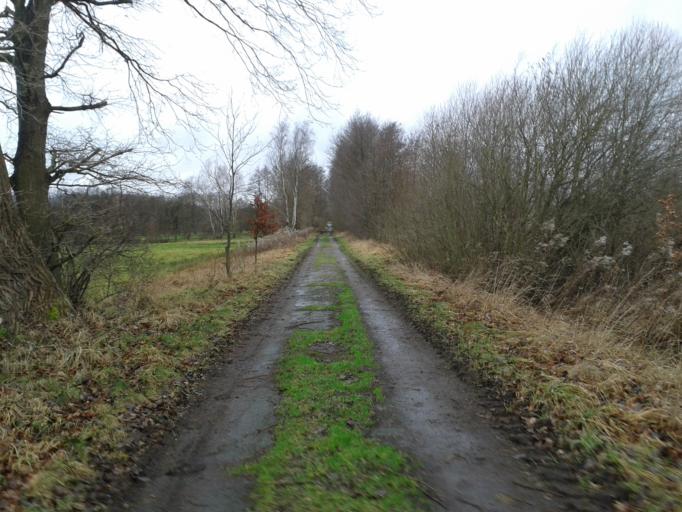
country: DE
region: Lower Saxony
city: Bergen an der Dumme
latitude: 52.9092
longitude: 10.9723
